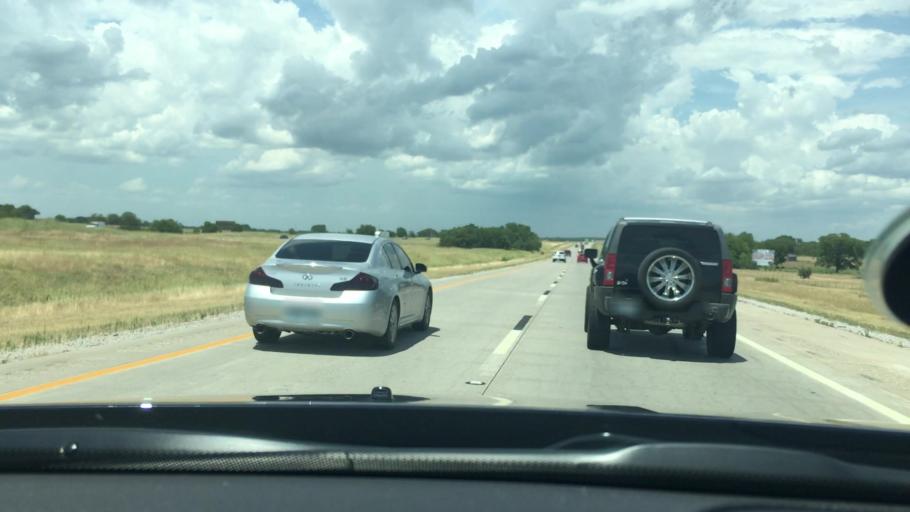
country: US
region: Oklahoma
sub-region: Carter County
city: Ardmore
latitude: 34.0884
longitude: -97.1501
